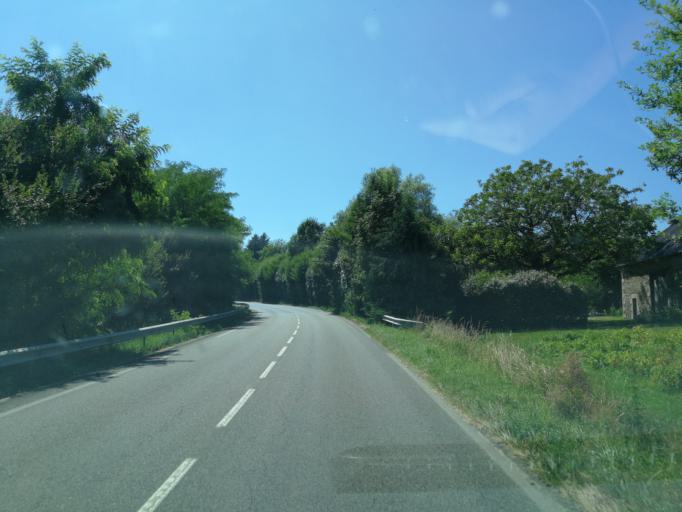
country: FR
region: Limousin
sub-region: Departement de la Correze
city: Sainte-Fereole
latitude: 45.2287
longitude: 1.5905
